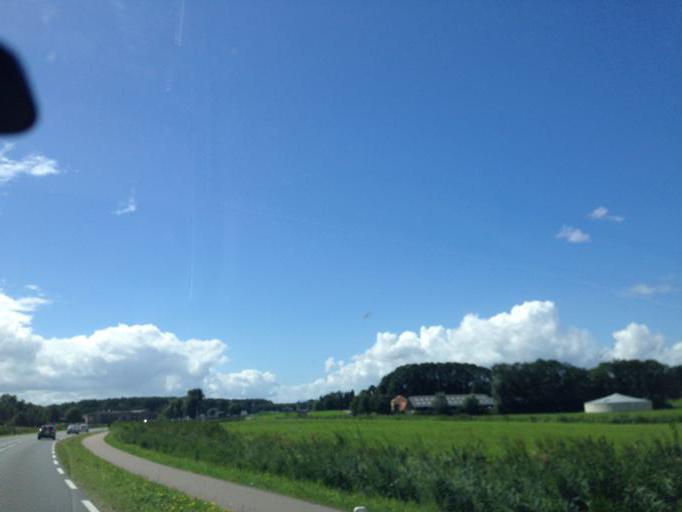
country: NL
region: Overijssel
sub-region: Gemeente Kampen
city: Kampen
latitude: 52.5472
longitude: 5.8653
